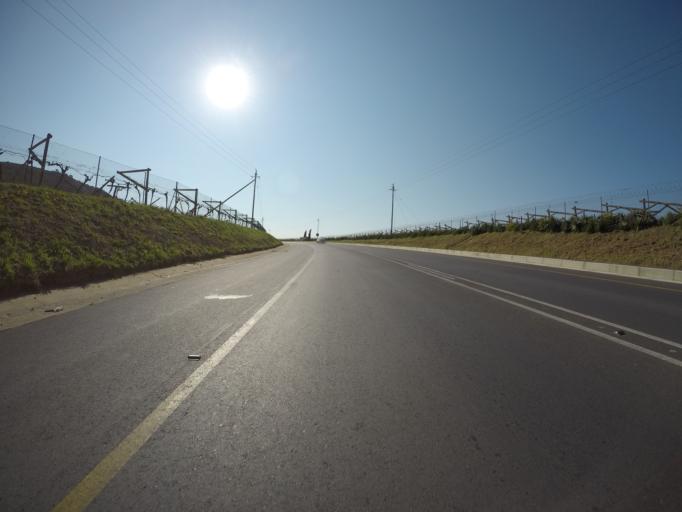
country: ZA
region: Western Cape
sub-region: Cape Winelands District Municipality
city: Noorder-Paarl
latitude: -33.6936
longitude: 18.9575
